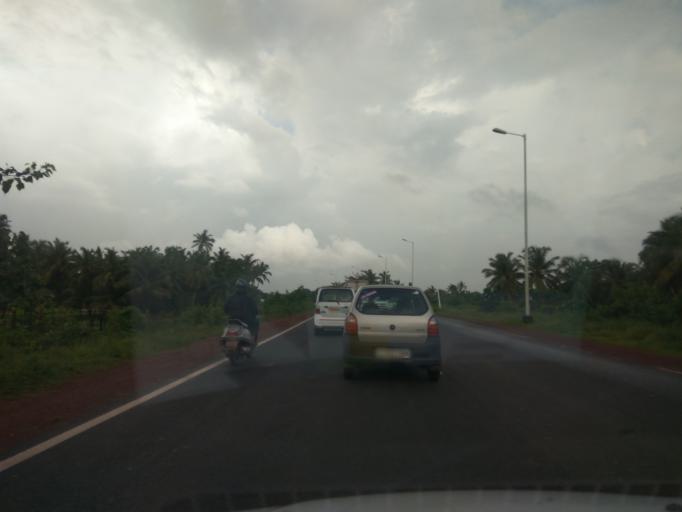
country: IN
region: Goa
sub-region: North Goa
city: Goa Velha
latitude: 15.4249
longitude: 73.8960
